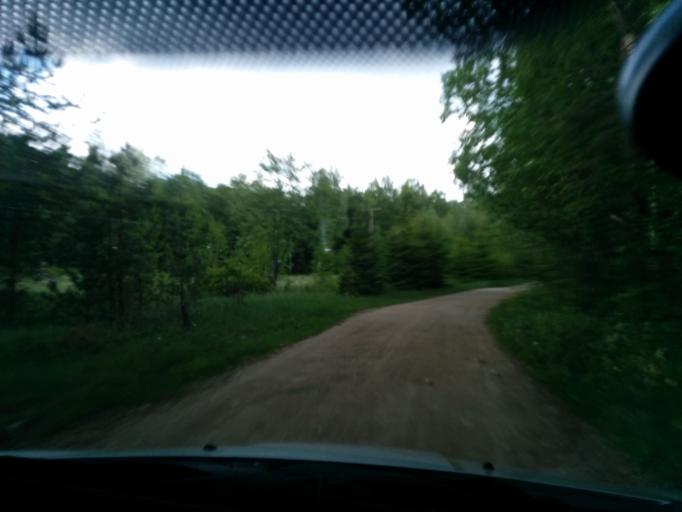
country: EE
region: Harju
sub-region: Loksa linn
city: Loksa
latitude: 59.6605
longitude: 25.7002
